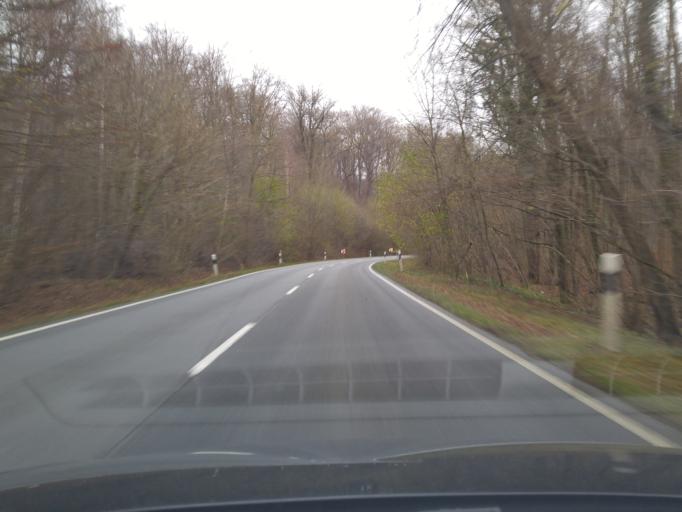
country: DE
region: Lower Saxony
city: Holle
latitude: 52.1250
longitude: 10.1535
